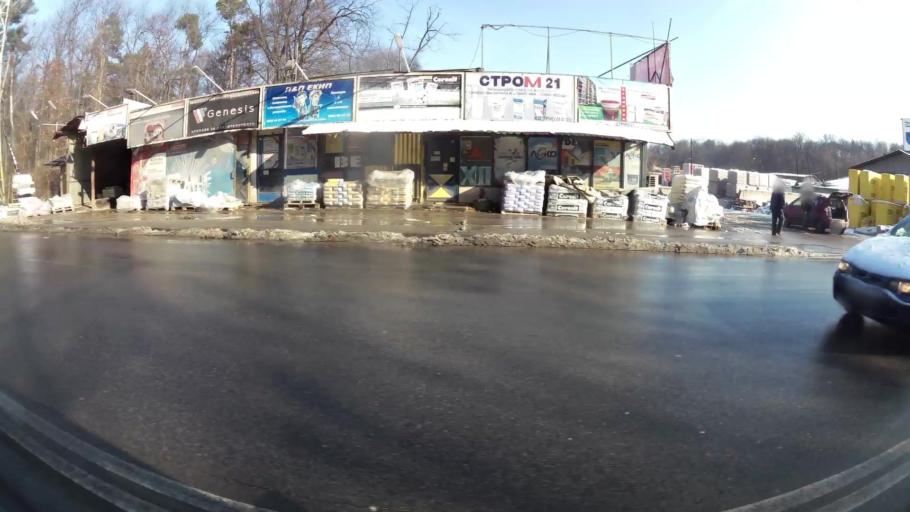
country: BG
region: Sofia-Capital
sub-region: Stolichna Obshtina
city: Sofia
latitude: 42.6673
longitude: 23.3376
